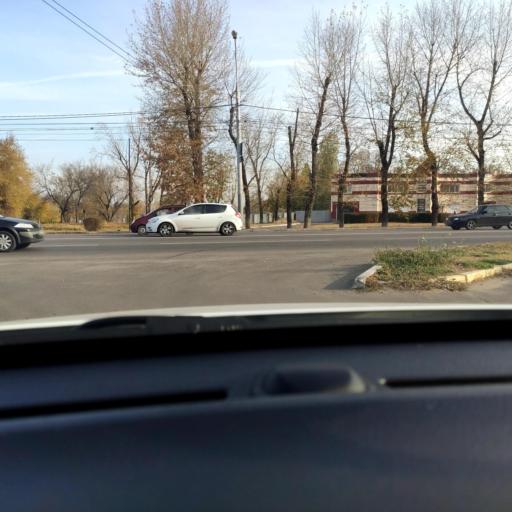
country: RU
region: Voronezj
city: Voronezh
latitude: 51.6573
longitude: 39.2852
